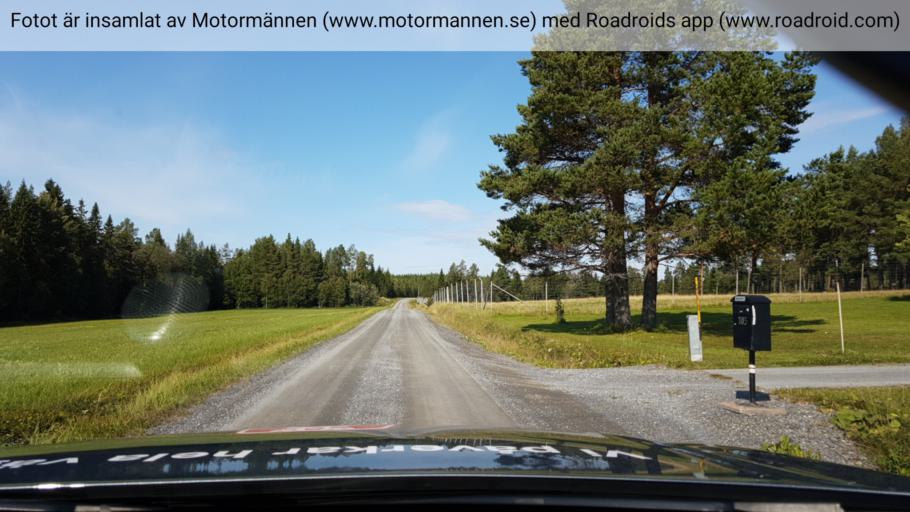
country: SE
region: Jaemtland
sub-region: OEstersunds Kommun
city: Ostersund
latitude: 63.1121
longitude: 14.4891
